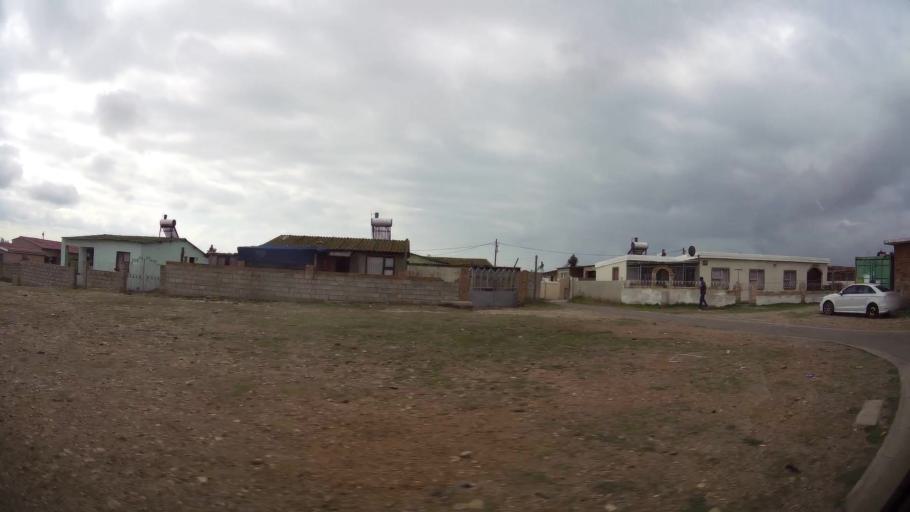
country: ZA
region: Eastern Cape
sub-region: Nelson Mandela Bay Metropolitan Municipality
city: Port Elizabeth
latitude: -33.8838
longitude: 25.6036
